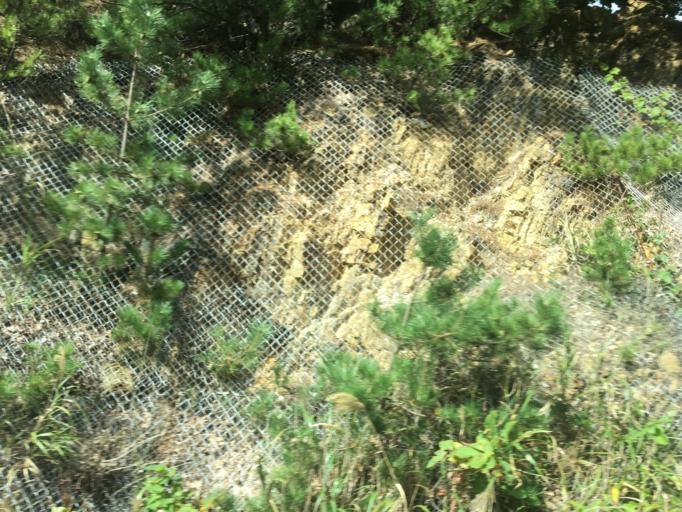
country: JP
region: Aomori
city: Shimokizukuri
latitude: 40.6635
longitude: 139.9378
